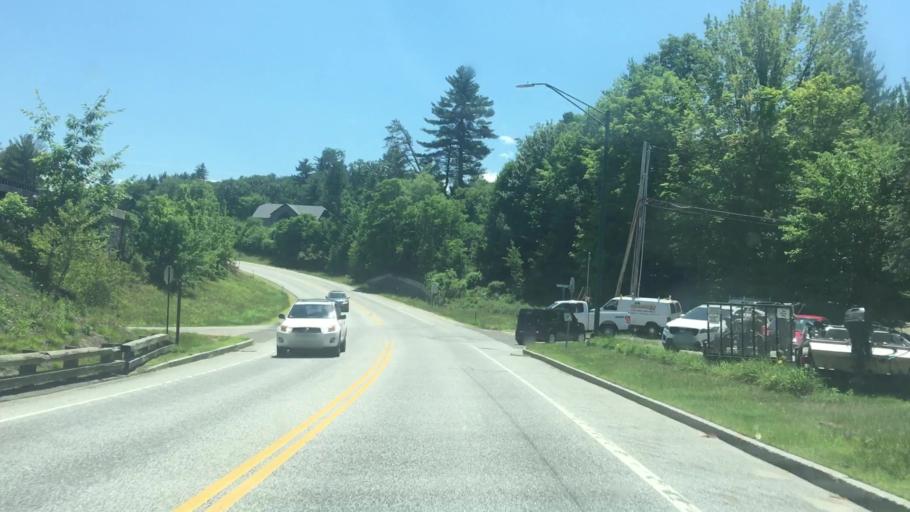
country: US
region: New Hampshire
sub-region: Carroll County
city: North Conway
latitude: 44.0451
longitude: -71.1223
